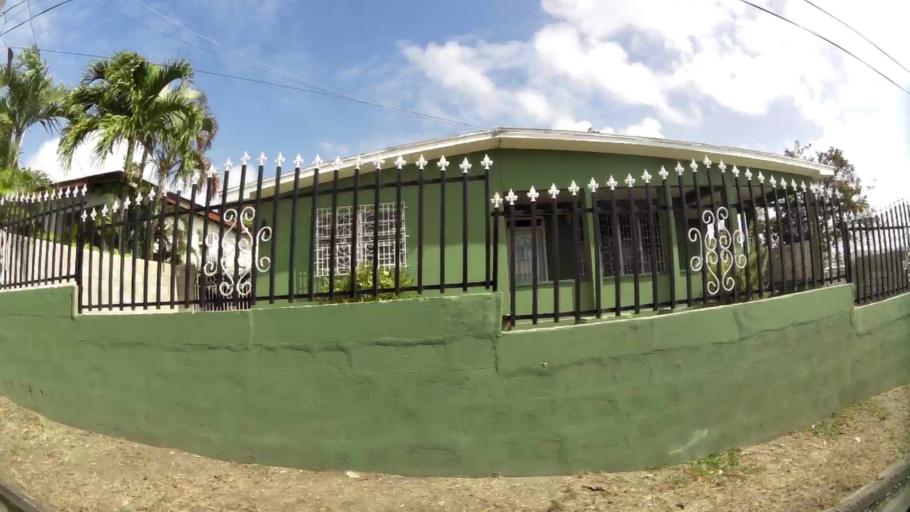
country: KN
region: Saint George Basseterre
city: Basseterre
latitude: 17.3017
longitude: -62.7298
